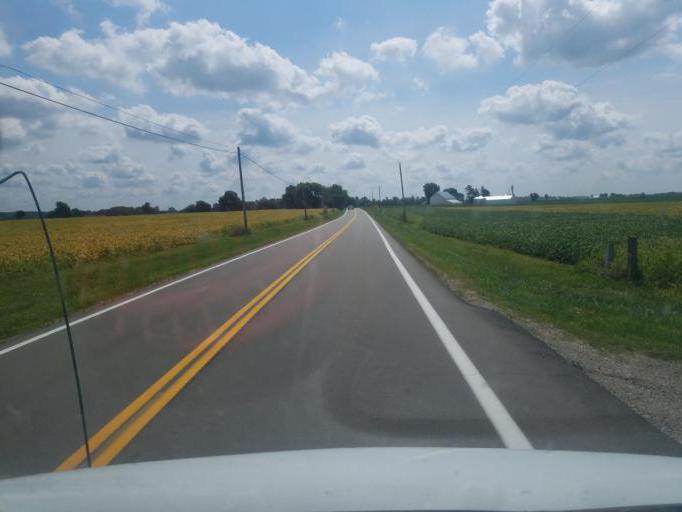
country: US
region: Ohio
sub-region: Marion County
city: Prospect
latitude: 40.4041
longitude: -83.1651
